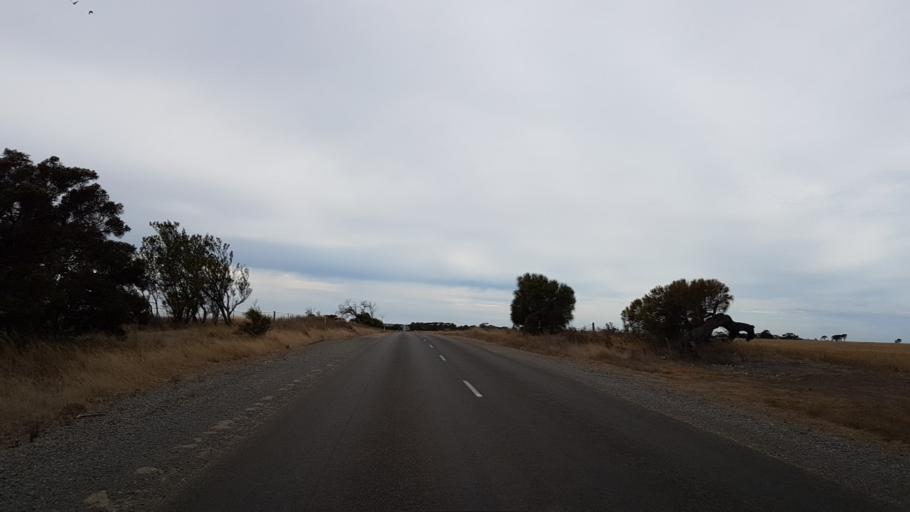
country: AU
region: South Australia
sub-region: Yorke Peninsula
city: Honiton
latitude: -34.9850
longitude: 137.3001
